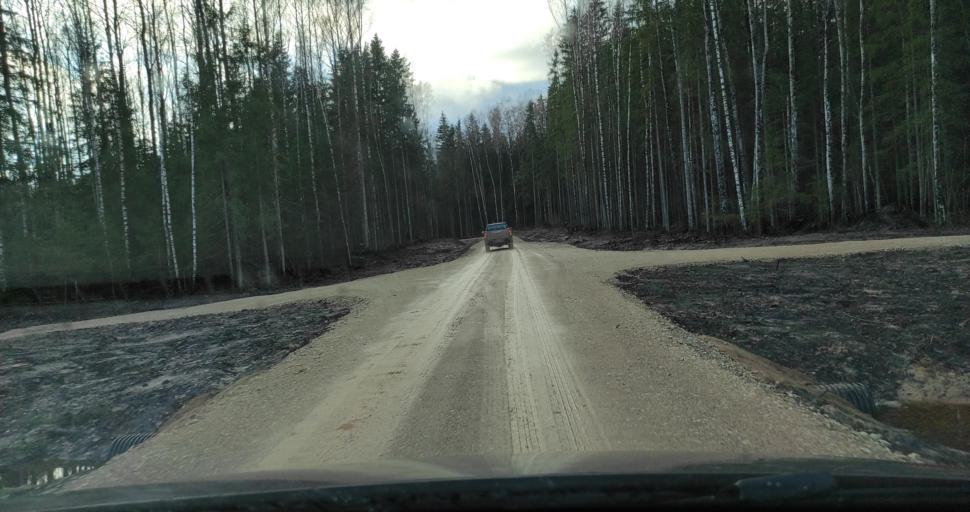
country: LV
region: Skrunda
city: Skrunda
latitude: 56.7426
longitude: 22.1948
